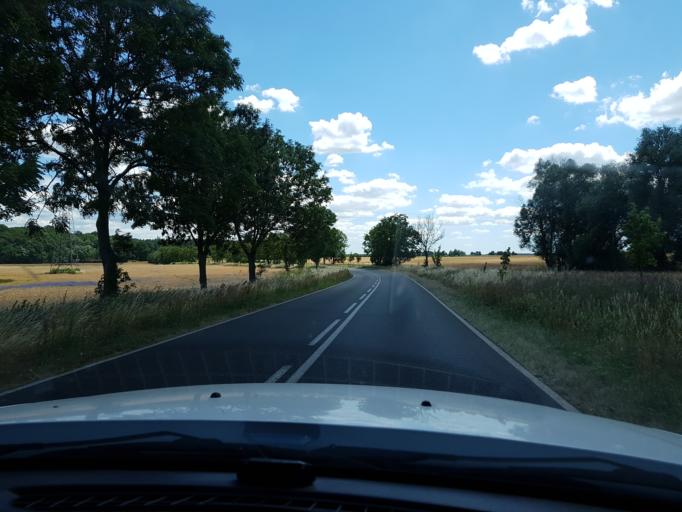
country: PL
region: West Pomeranian Voivodeship
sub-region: Powiat mysliborski
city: Mysliborz
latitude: 52.9158
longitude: 14.9084
